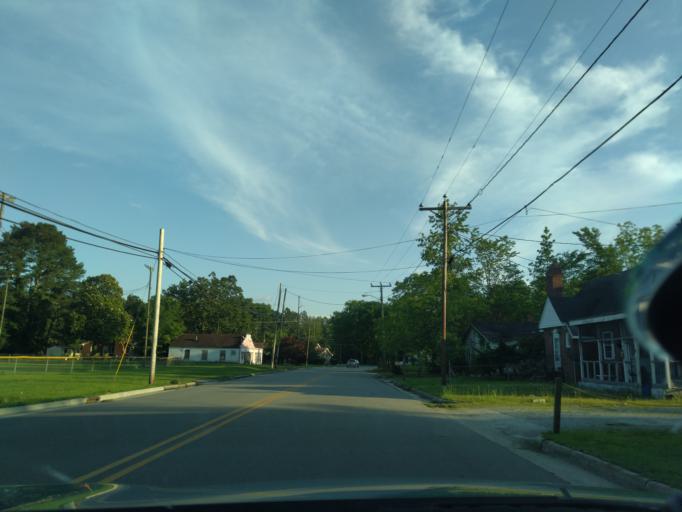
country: US
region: North Carolina
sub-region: Washington County
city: Plymouth
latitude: 35.8583
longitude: -76.7541
